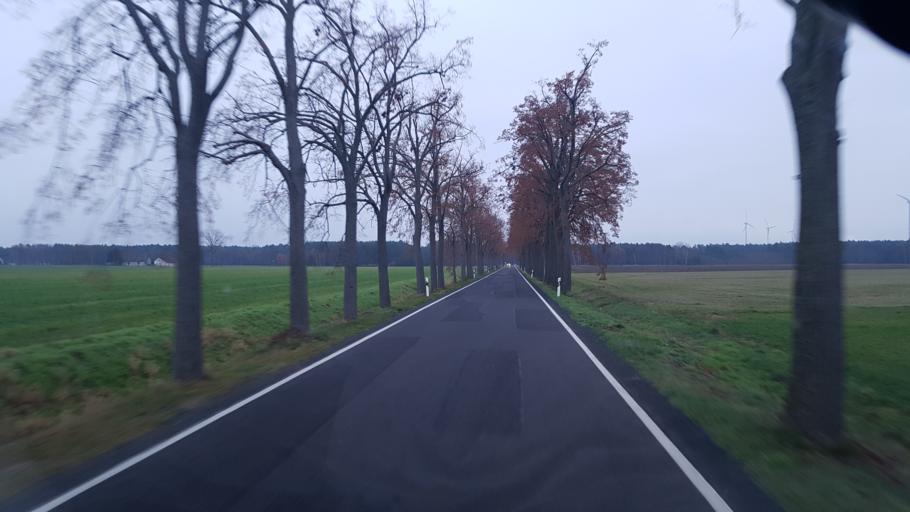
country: DE
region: Brandenburg
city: Drachhausen
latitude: 51.8917
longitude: 14.3353
